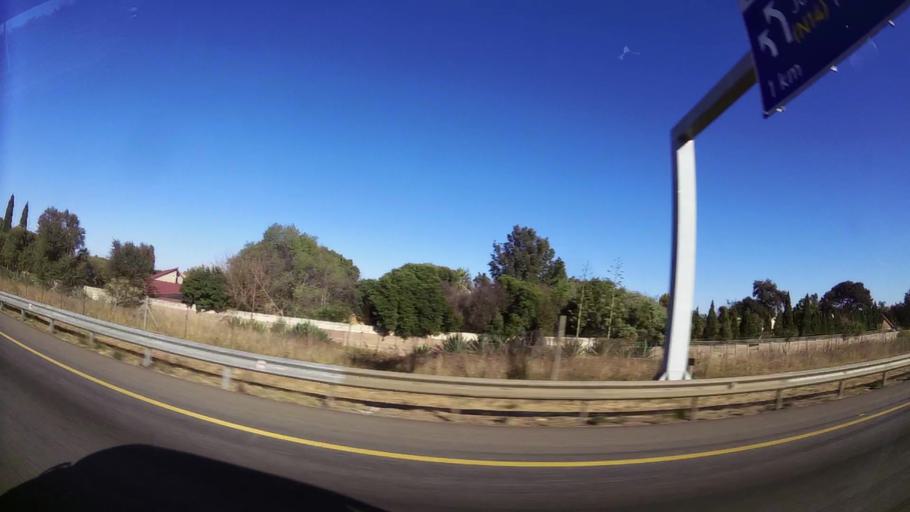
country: ZA
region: Gauteng
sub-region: City of Tshwane Metropolitan Municipality
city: Centurion
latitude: -25.8440
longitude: 28.2497
